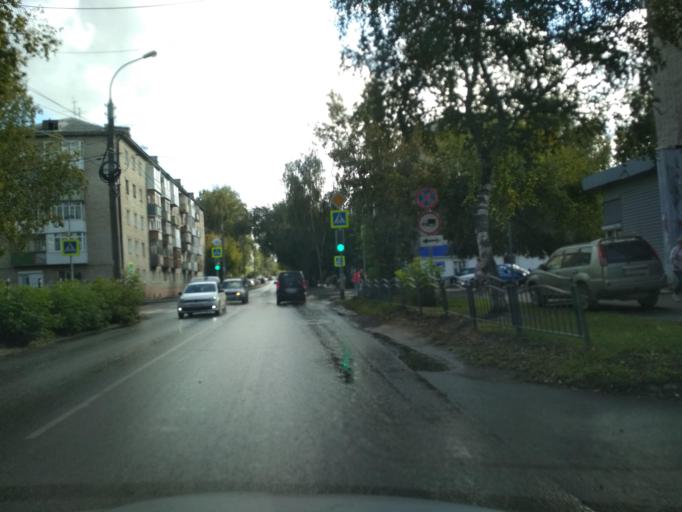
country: RU
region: Tomsk
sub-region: Tomskiy Rayon
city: Tomsk
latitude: 56.4694
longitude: 84.9756
